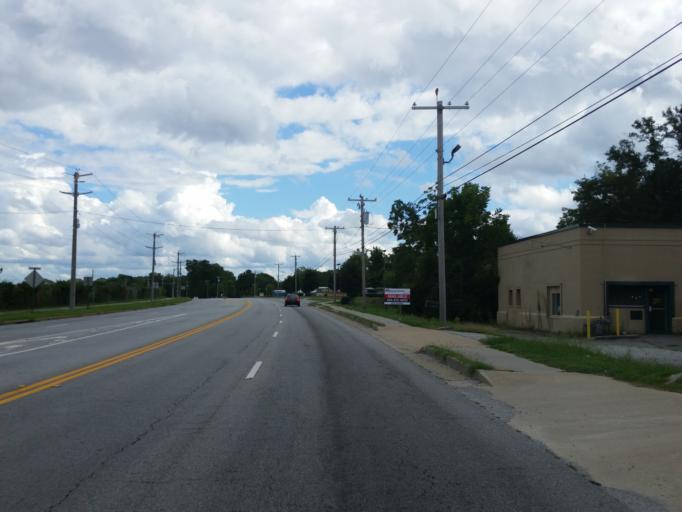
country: US
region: Georgia
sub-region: Cobb County
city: Fair Oaks
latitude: 33.9207
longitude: -84.5426
